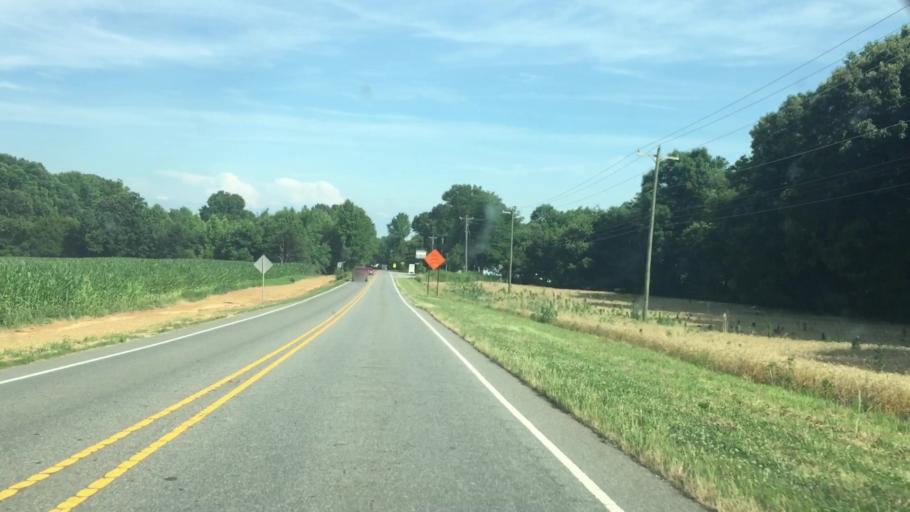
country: US
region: North Carolina
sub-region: Iredell County
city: Mooresville
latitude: 35.5599
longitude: -80.7874
